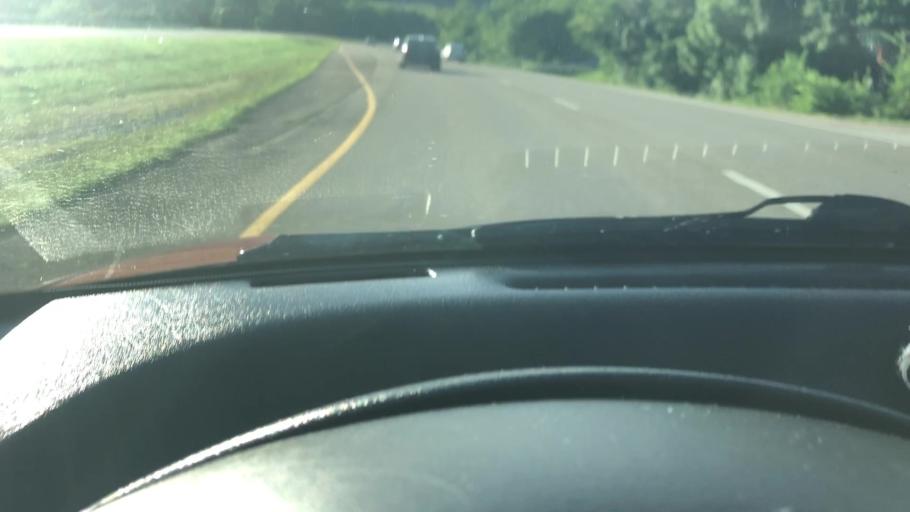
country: US
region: Tennessee
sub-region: Jefferson County
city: Jefferson City
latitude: 36.0622
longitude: -83.4768
